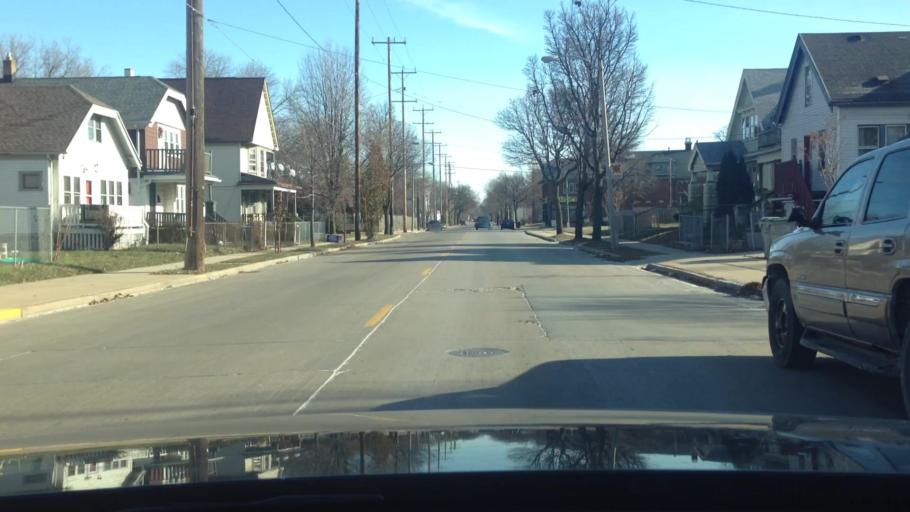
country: US
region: Wisconsin
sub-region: Milwaukee County
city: Shorewood
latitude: 43.0821
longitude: -87.9122
